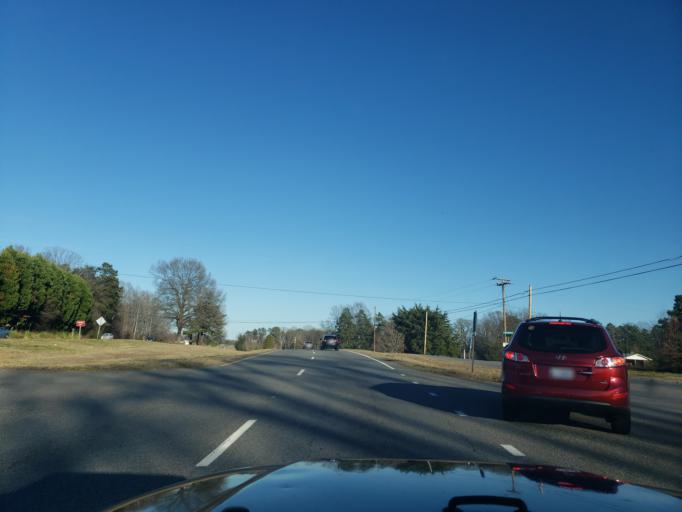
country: US
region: North Carolina
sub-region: Gaston County
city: Bessemer City
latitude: 35.2489
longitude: -81.2858
